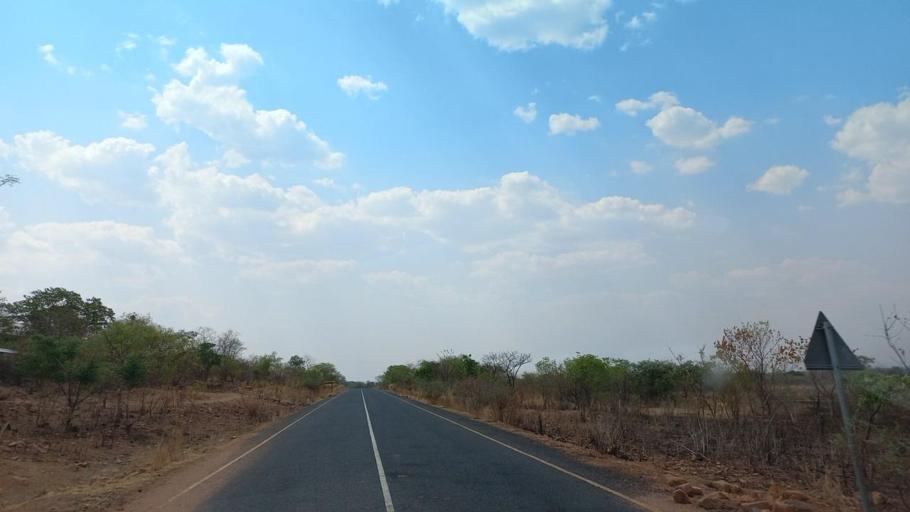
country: ZM
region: Lusaka
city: Luangwa
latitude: -15.3238
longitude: 30.3407
